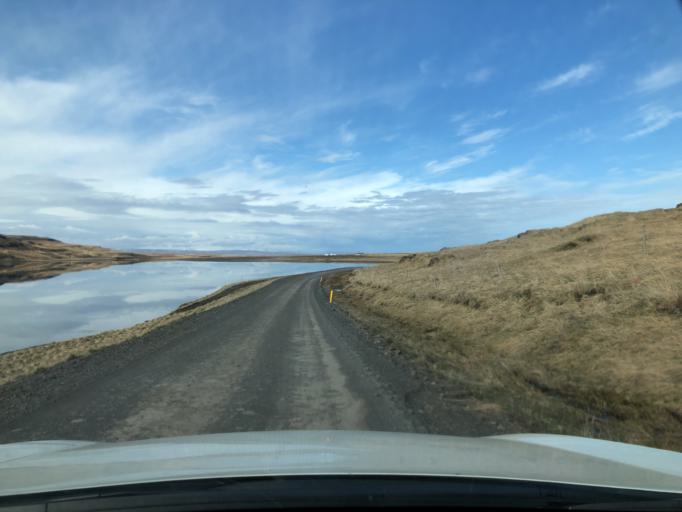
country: IS
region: West
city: Borgarnes
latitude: 65.0562
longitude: -21.6438
